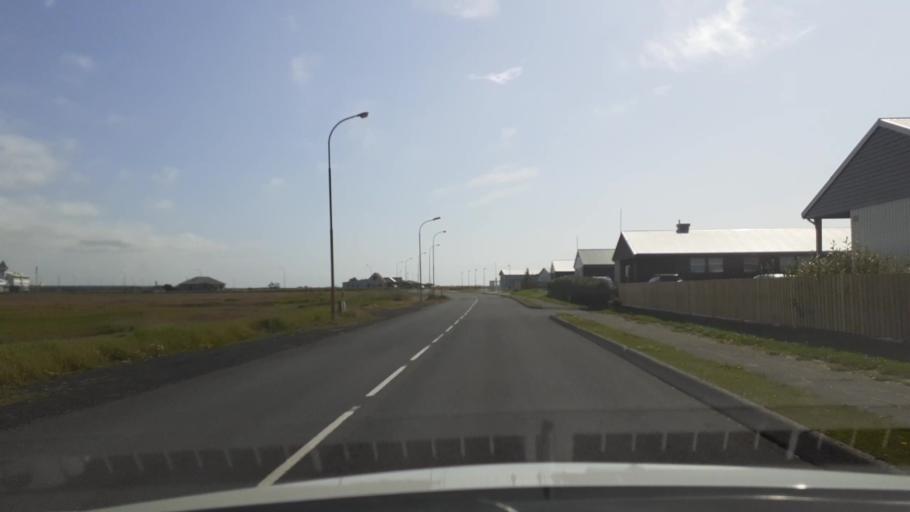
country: IS
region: South
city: Hveragerdi
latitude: 63.8594
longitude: -21.1375
